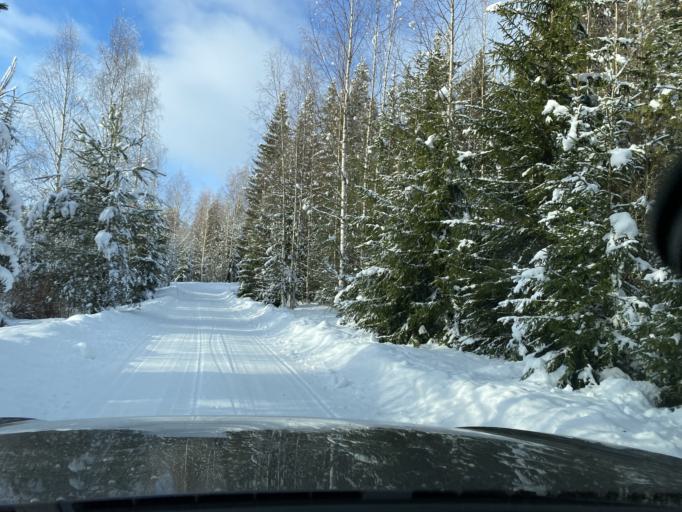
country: FI
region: Pirkanmaa
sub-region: Lounais-Pirkanmaa
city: Punkalaidun
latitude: 61.0715
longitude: 23.2387
